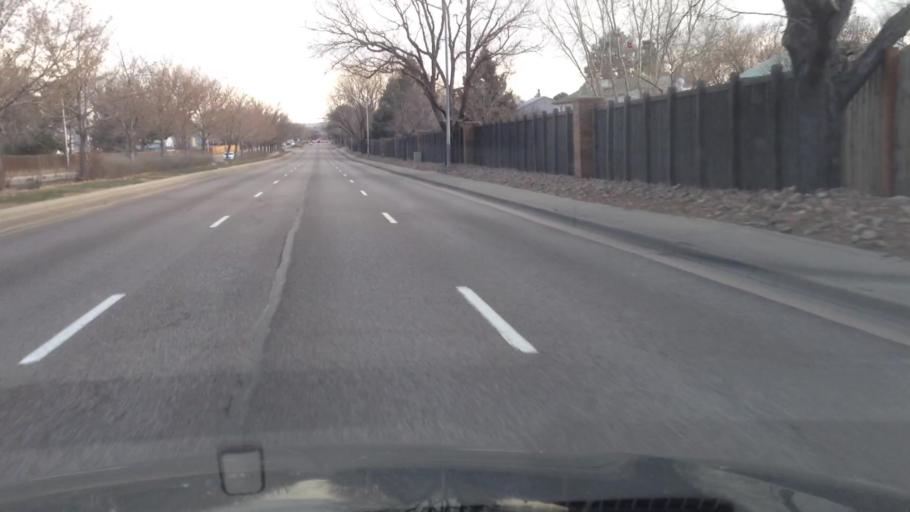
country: US
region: Colorado
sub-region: Adams County
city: Aurora
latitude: 39.6748
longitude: -104.8187
